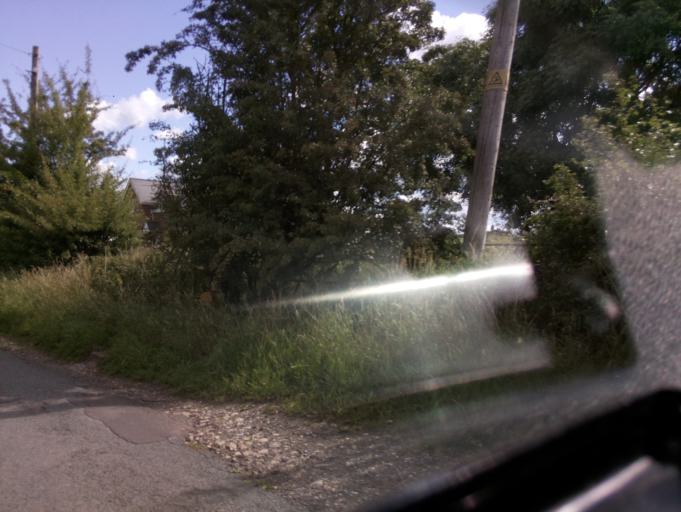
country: GB
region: England
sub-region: Gloucestershire
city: Newent
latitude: 51.8588
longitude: -2.3531
